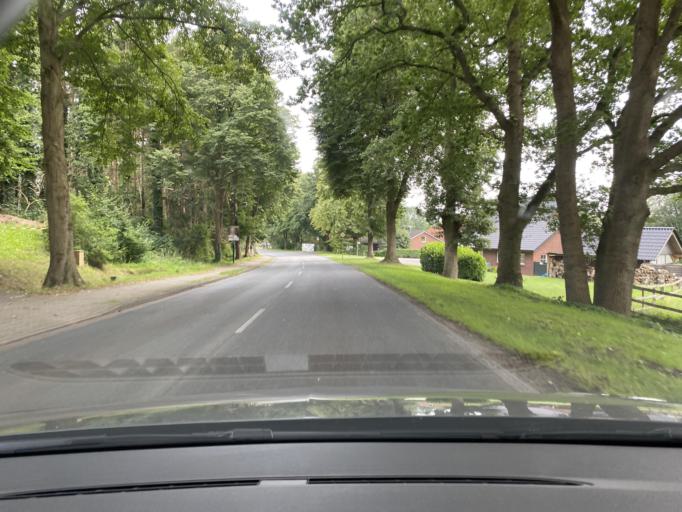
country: DE
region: Lower Saxony
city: Vollersode
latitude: 53.3217
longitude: 8.8994
